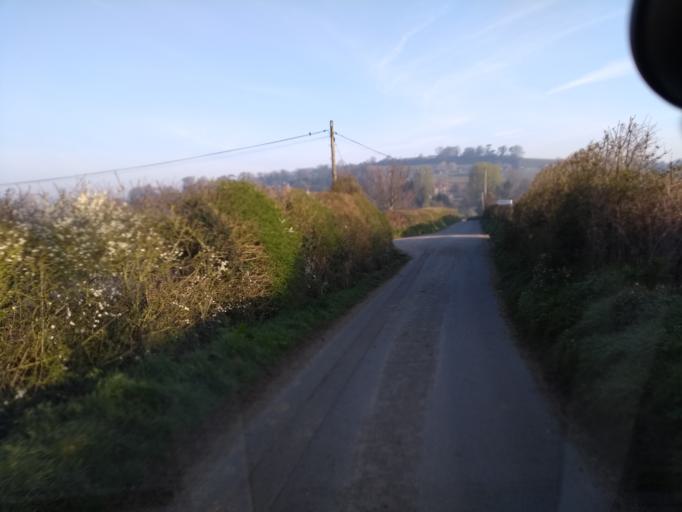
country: GB
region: England
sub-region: Somerset
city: Crewkerne
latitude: 50.8461
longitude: -2.8105
